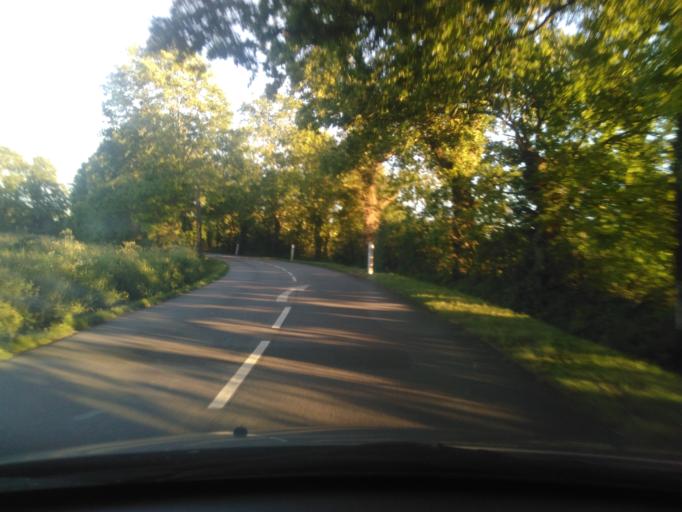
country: FR
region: Pays de la Loire
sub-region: Departement de la Vendee
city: Nesmy
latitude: 46.6134
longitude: -1.4136
